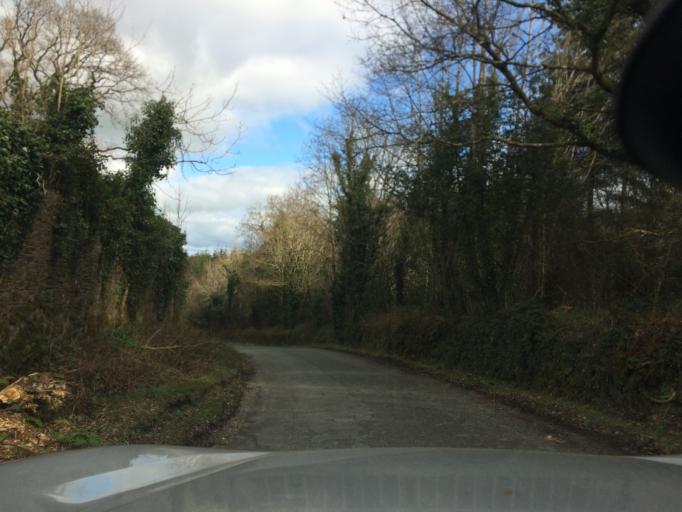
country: IE
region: Munster
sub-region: Waterford
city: Portlaw
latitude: 52.2854
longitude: -7.3389
